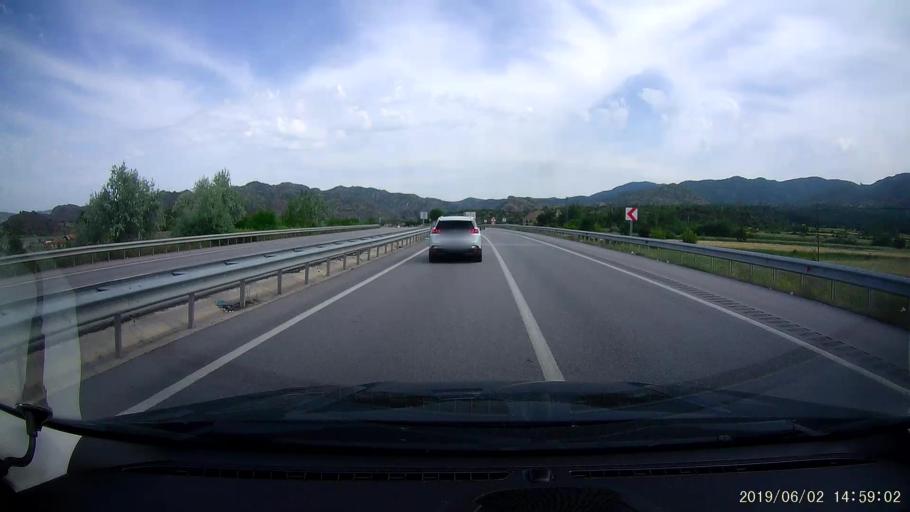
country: TR
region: Corum
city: Osmancik
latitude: 40.9732
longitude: 34.6891
